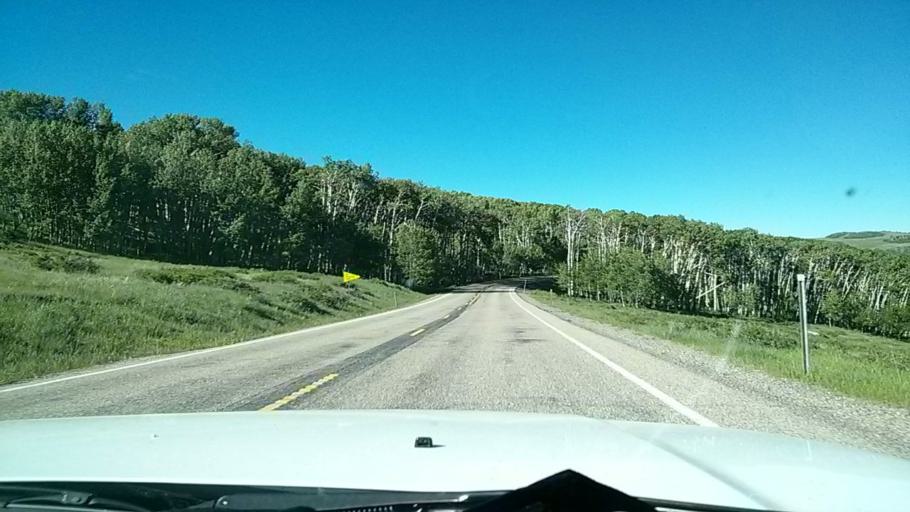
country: US
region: Utah
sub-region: Wayne County
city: Loa
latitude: 38.0158
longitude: -111.3569
